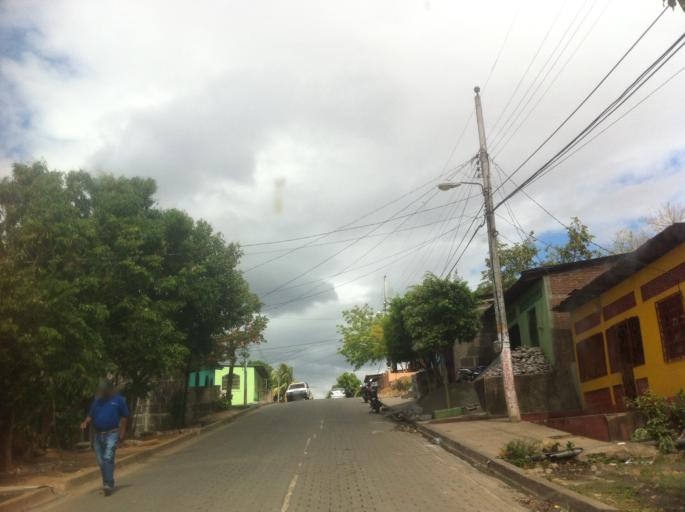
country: NI
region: Chontales
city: Juigalpa
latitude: 12.0987
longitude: -85.3615
